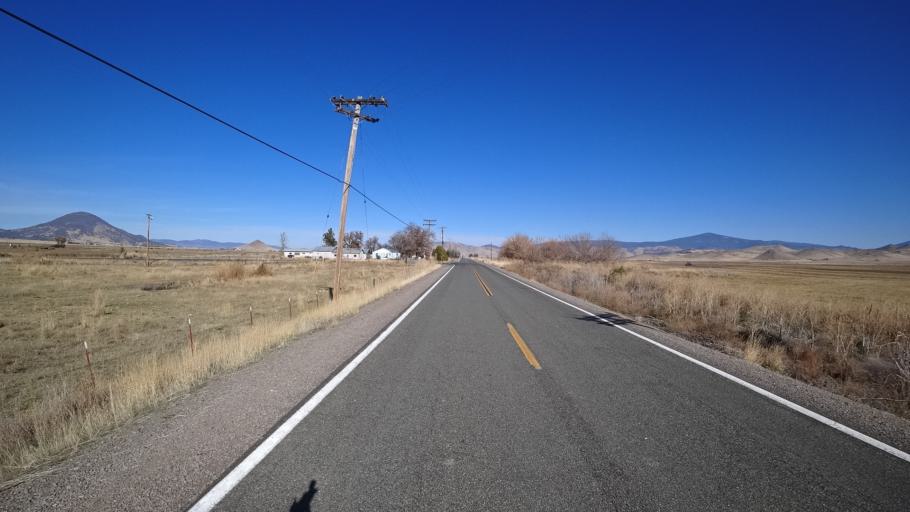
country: US
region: California
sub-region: Siskiyou County
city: Montague
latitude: 41.7698
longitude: -122.4816
